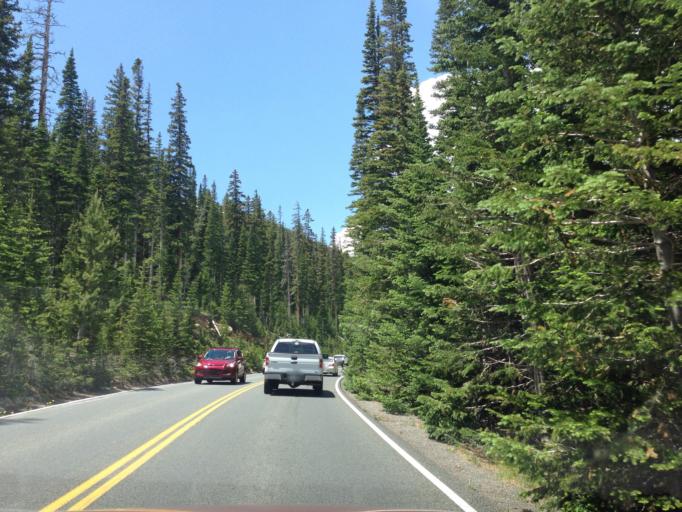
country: US
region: Colorado
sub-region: Larimer County
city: Estes Park
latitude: 40.3855
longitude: -105.6627
